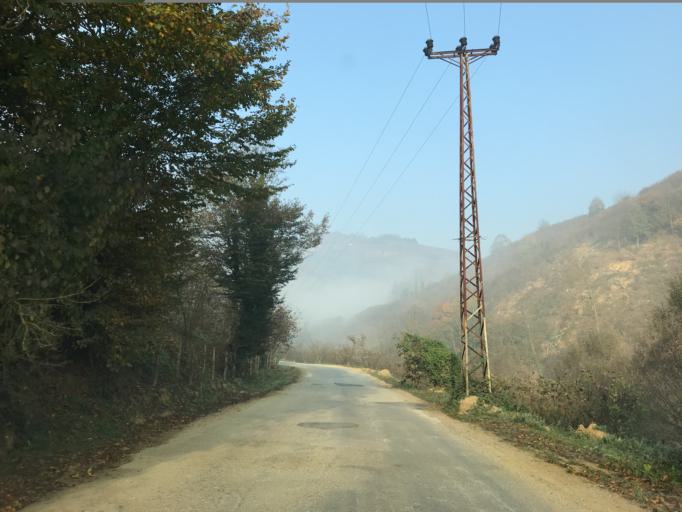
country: TR
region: Duzce
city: Cumayeri
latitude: 40.9163
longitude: 30.9349
